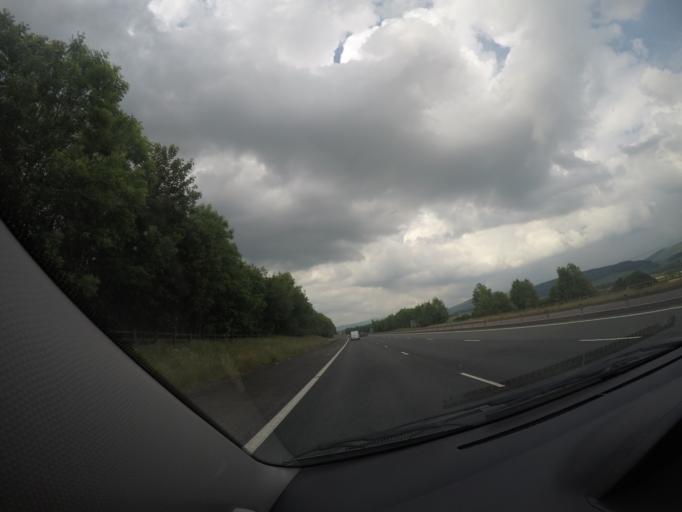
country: GB
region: Scotland
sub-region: Dumfries and Galloway
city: Moffat
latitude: 55.2462
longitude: -3.4095
